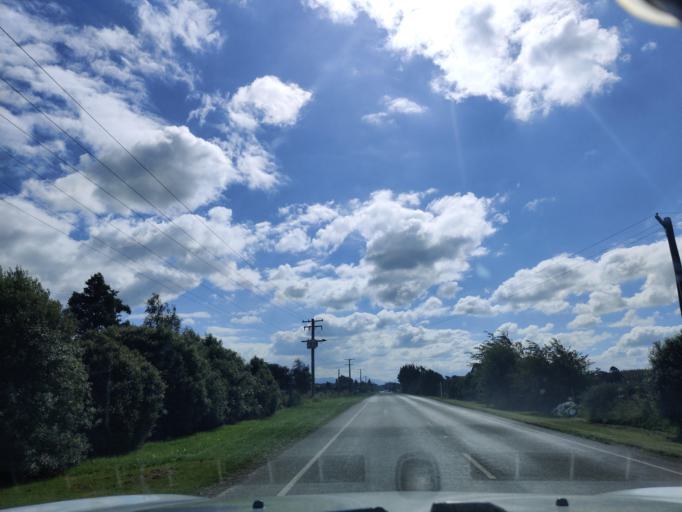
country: NZ
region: Canterbury
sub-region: Timaru District
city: Pleasant Point
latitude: -44.1312
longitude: 171.2917
